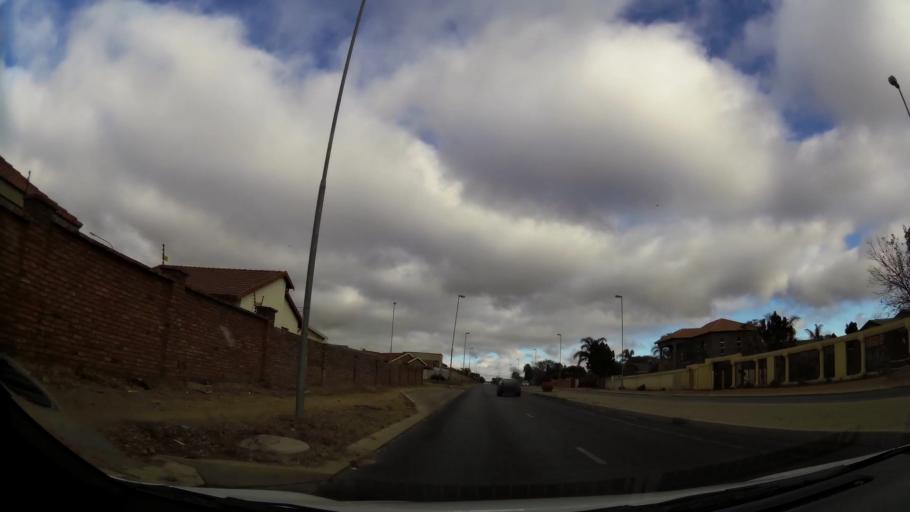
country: ZA
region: Limpopo
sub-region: Capricorn District Municipality
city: Polokwane
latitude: -23.9204
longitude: 29.4427
